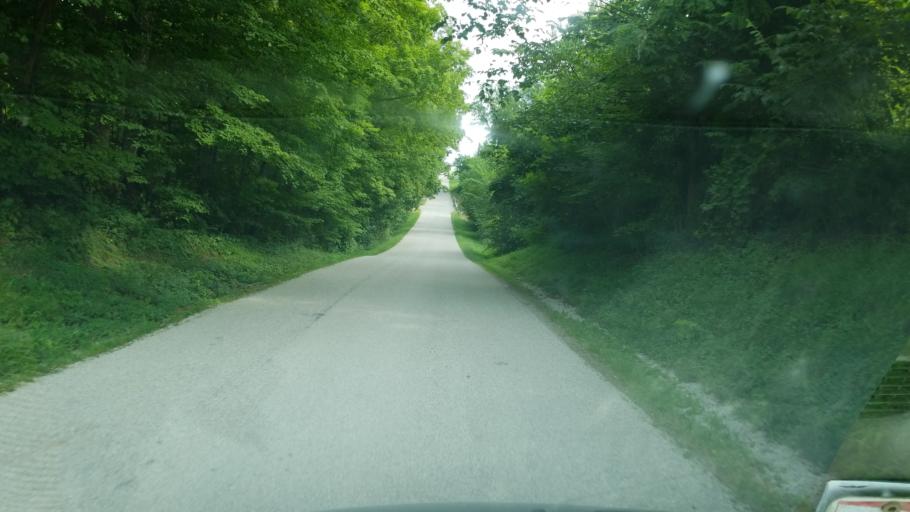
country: US
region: Ohio
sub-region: Seneca County
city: Tiffin
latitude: 41.1536
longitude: -83.0947
